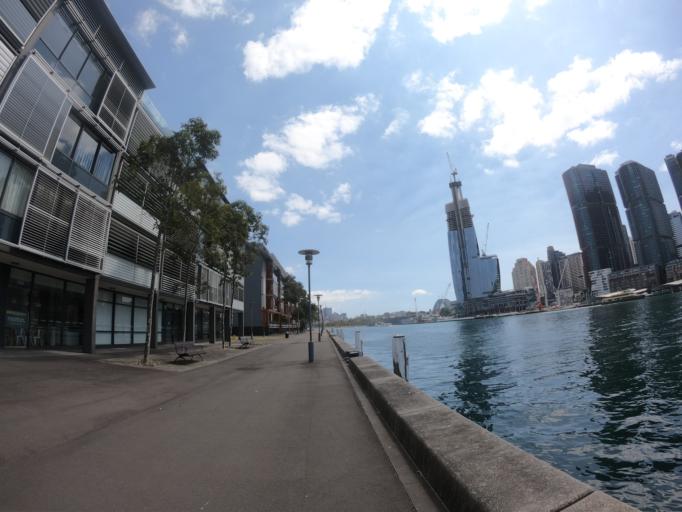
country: AU
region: New South Wales
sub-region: Leichhardt
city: Balmain East
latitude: -33.8653
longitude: 151.1969
